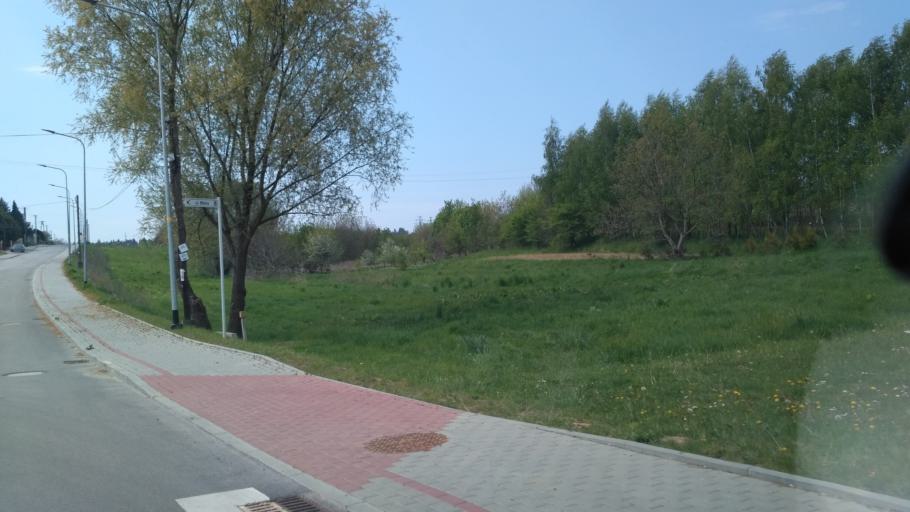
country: PL
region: Subcarpathian Voivodeship
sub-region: Powiat jaroslawski
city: Jaroslaw
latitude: 50.0052
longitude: 22.6818
